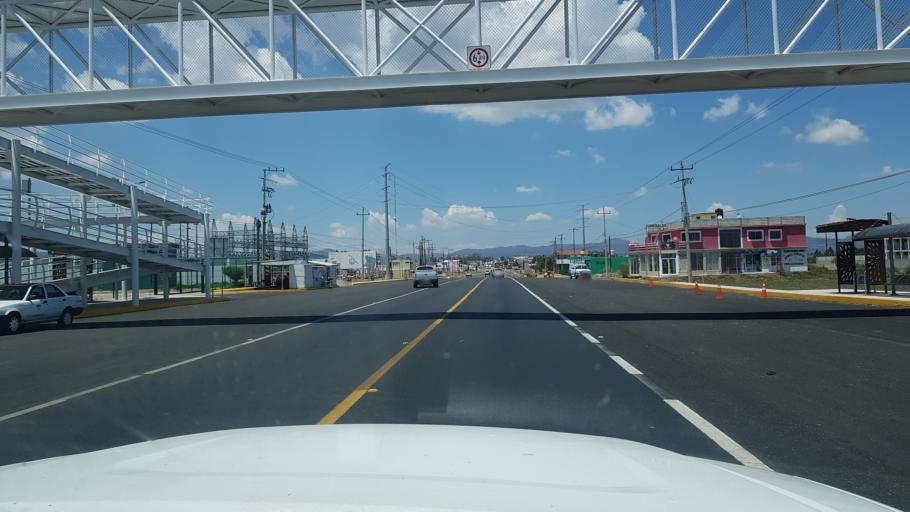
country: MX
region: Hidalgo
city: Calpulalpan
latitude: 19.5833
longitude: -98.5366
